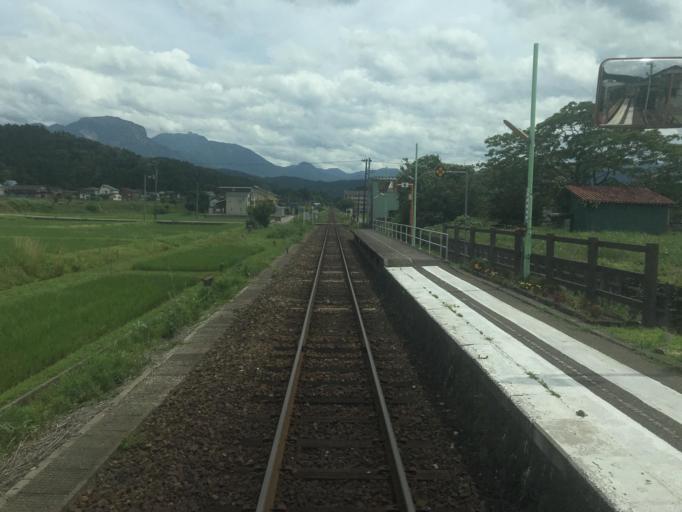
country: JP
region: Niigata
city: Itoigawa
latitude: 37.0059
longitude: 137.8726
